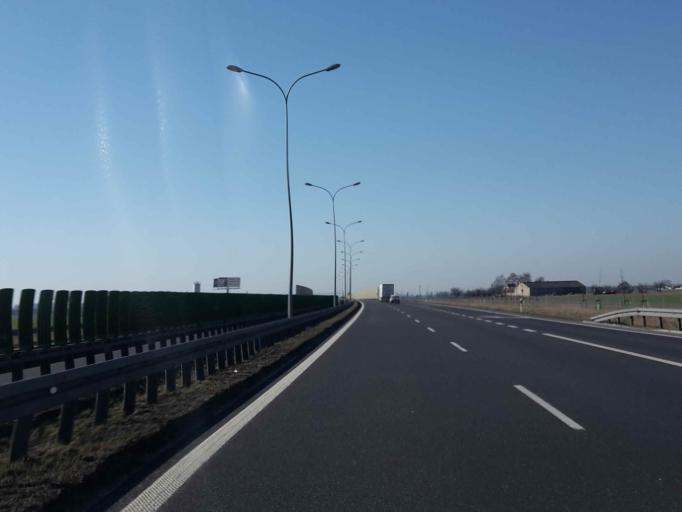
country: PL
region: Greater Poland Voivodeship
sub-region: Powiat poznanski
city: Kleszczewo
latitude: 52.3393
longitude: 17.1612
